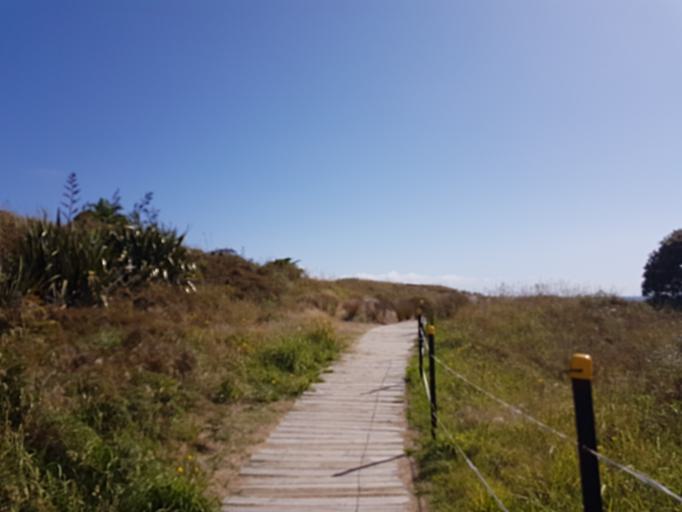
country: NZ
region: Bay of Plenty
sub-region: Tauranga City
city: Tauranga
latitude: -37.7065
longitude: 176.3129
